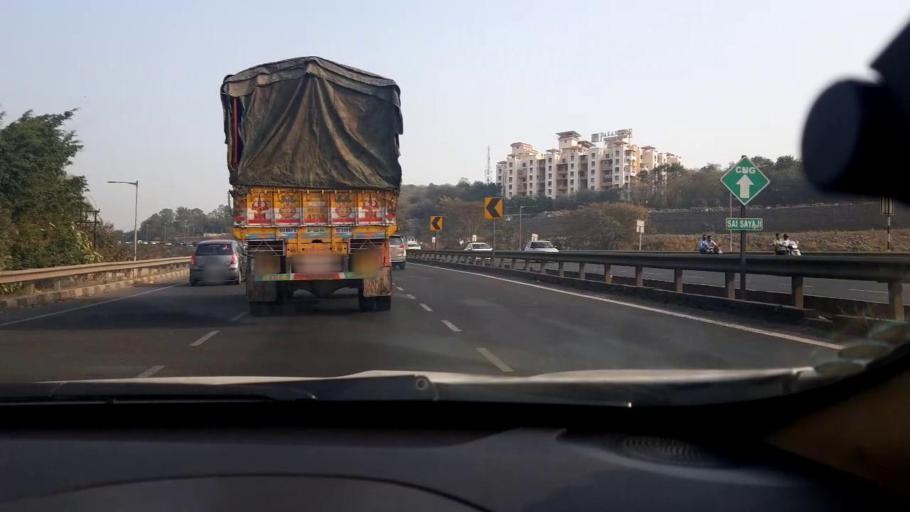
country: IN
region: Maharashtra
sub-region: Pune Division
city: Kharakvasla
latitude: 18.5100
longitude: 73.7733
